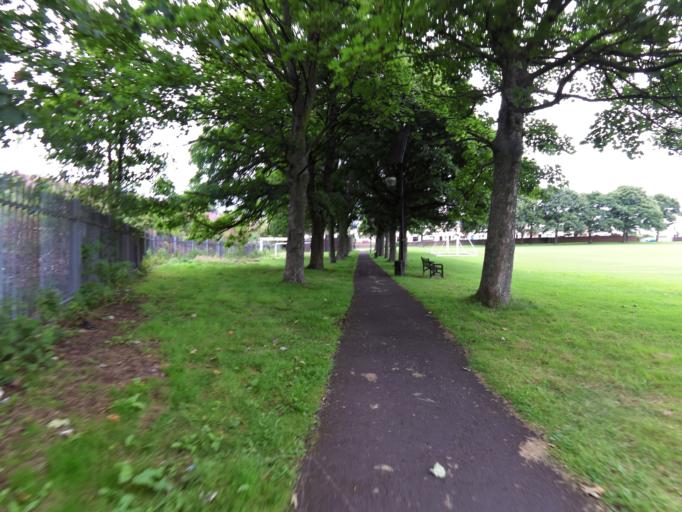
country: GB
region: Scotland
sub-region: East Lothian
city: Musselburgh
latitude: 55.9326
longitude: -3.0899
